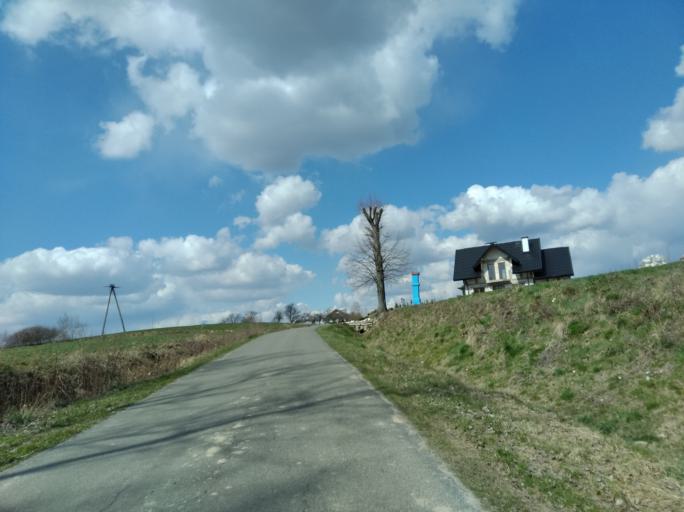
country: PL
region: Subcarpathian Voivodeship
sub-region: Powiat strzyzowski
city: Wisniowa
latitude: 49.9292
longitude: 21.7018
